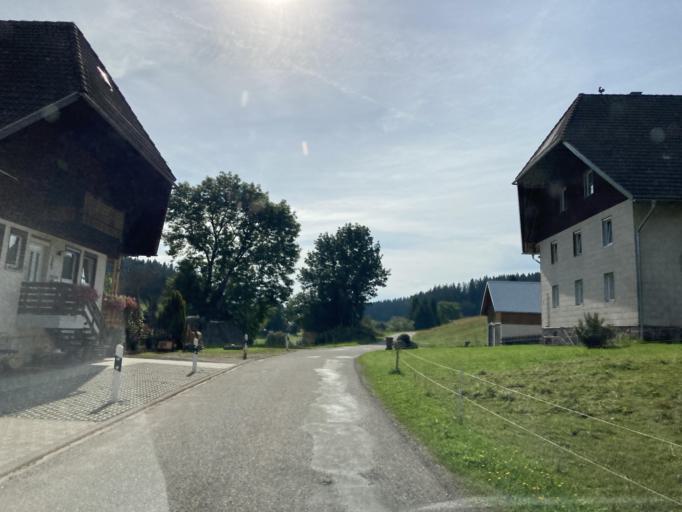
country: DE
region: Baden-Wuerttemberg
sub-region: Freiburg Region
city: Schonwald im Schwarzwald
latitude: 48.1002
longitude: 8.2133
